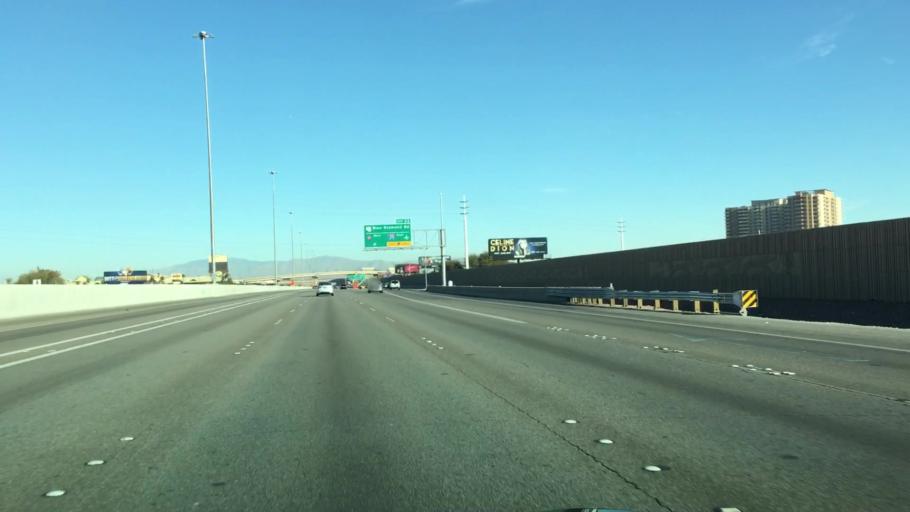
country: US
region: Nevada
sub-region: Clark County
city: Enterprise
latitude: 36.0334
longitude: -115.1805
